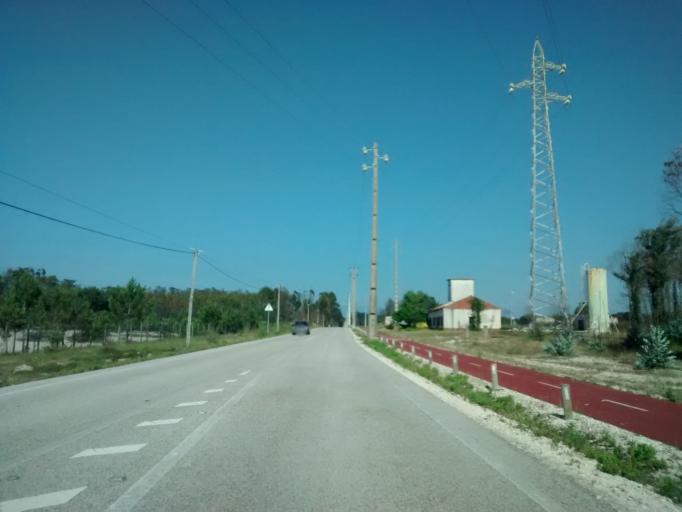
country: PT
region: Leiria
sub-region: Leiria
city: Monte Redondo
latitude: 39.9797
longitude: -8.8511
